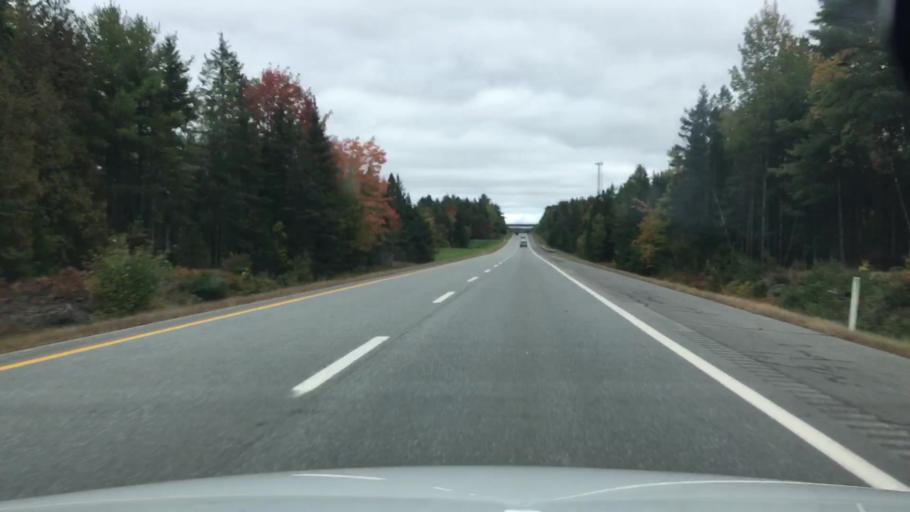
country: US
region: Maine
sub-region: Penobscot County
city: Plymouth
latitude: 44.7885
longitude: -69.1734
